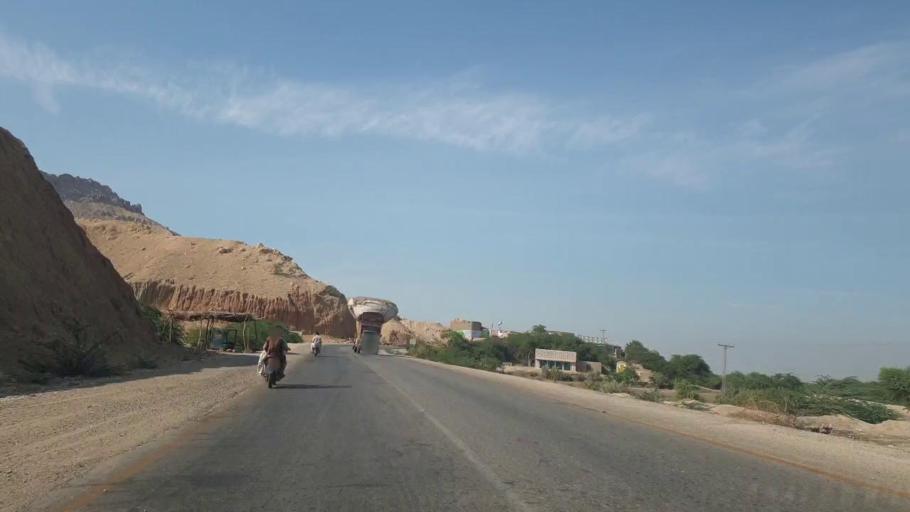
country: PK
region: Sindh
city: Sehwan
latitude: 26.3149
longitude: 67.8906
